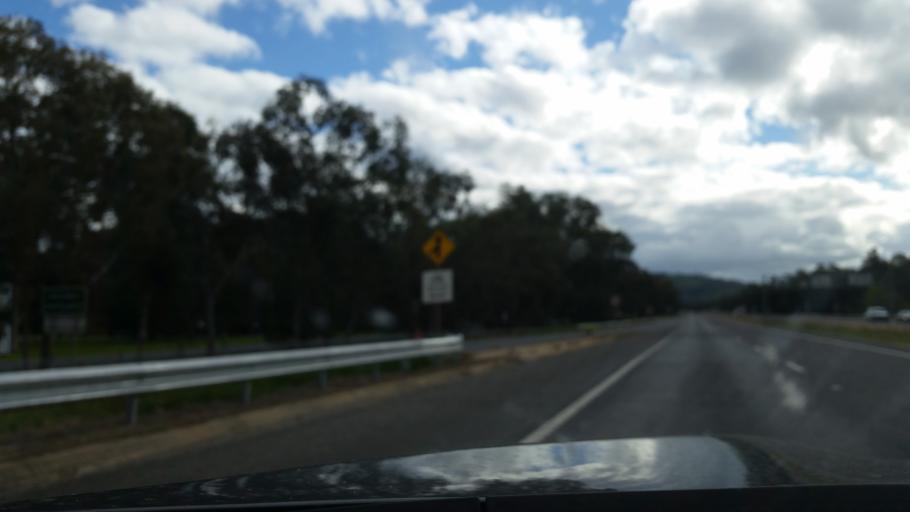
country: AU
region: Victoria
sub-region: Wodonga
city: Wodonga
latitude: -36.1091
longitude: 146.8556
